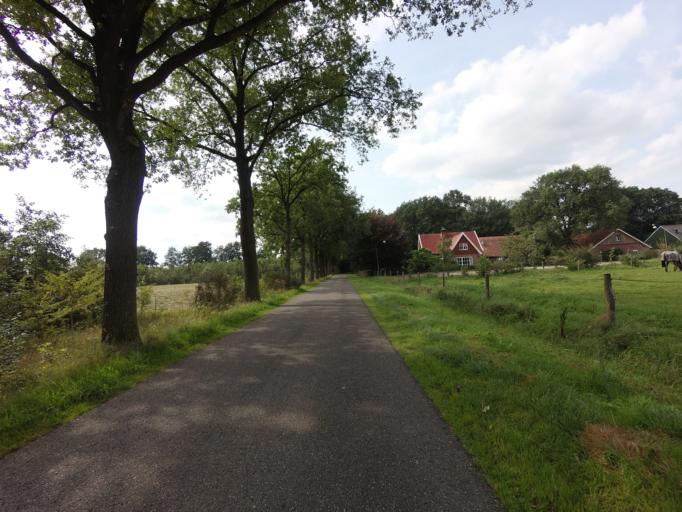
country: DE
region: Lower Saxony
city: Lage
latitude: 52.4307
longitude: 6.9307
